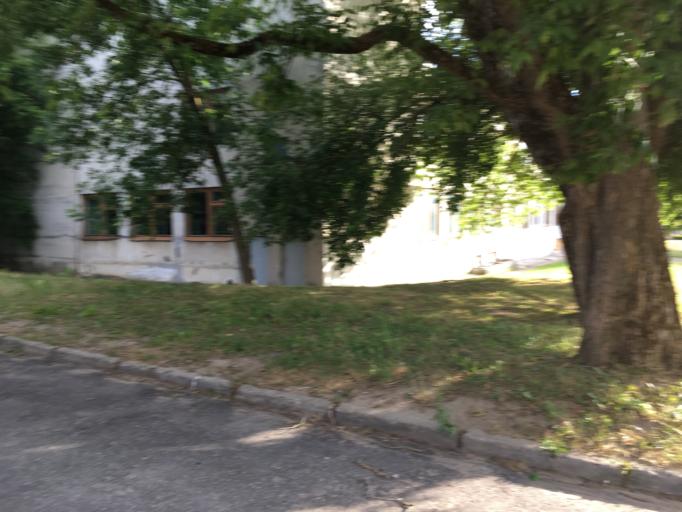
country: BY
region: Grodnenskaya
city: Hrodna
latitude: 53.7022
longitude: 23.8203
